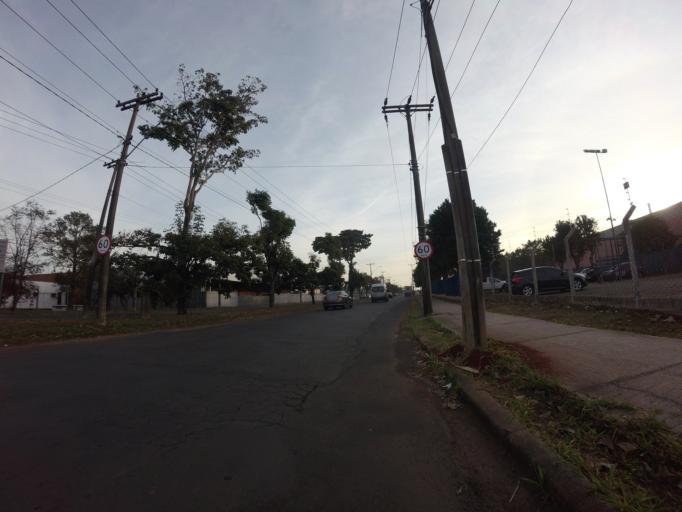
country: BR
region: Sao Paulo
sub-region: Piracicaba
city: Piracicaba
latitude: -22.7384
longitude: -47.5900
